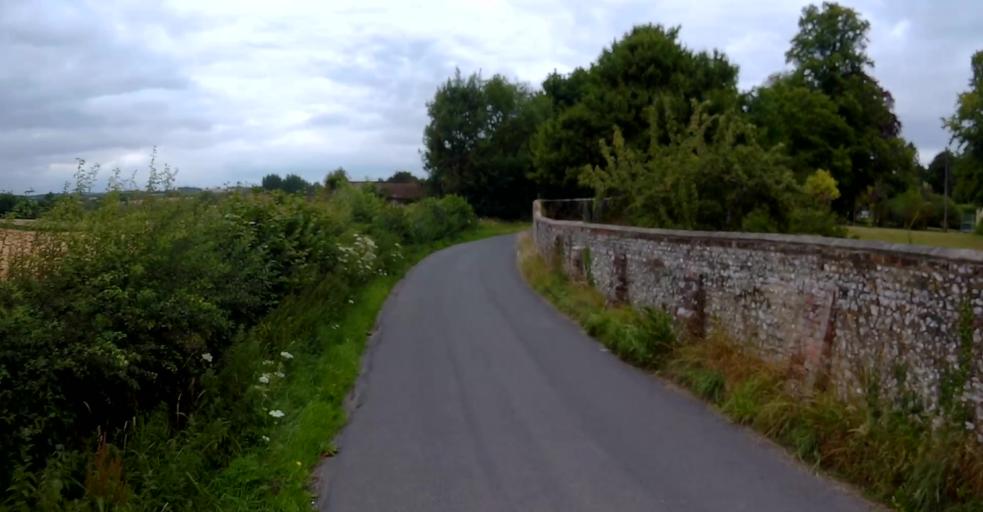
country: GB
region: England
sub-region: Hampshire
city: Kings Worthy
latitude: 51.0796
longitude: -1.2027
